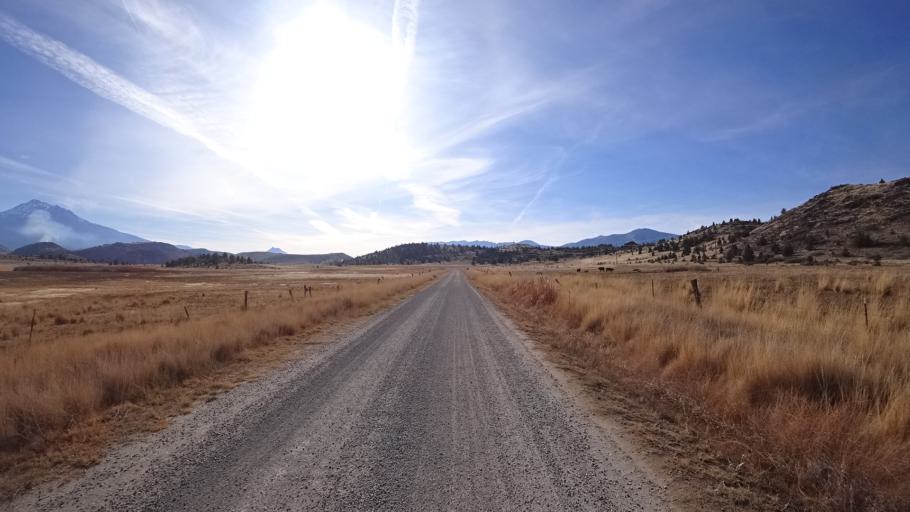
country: US
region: California
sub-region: Siskiyou County
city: Weed
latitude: 41.5445
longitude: -122.4726
